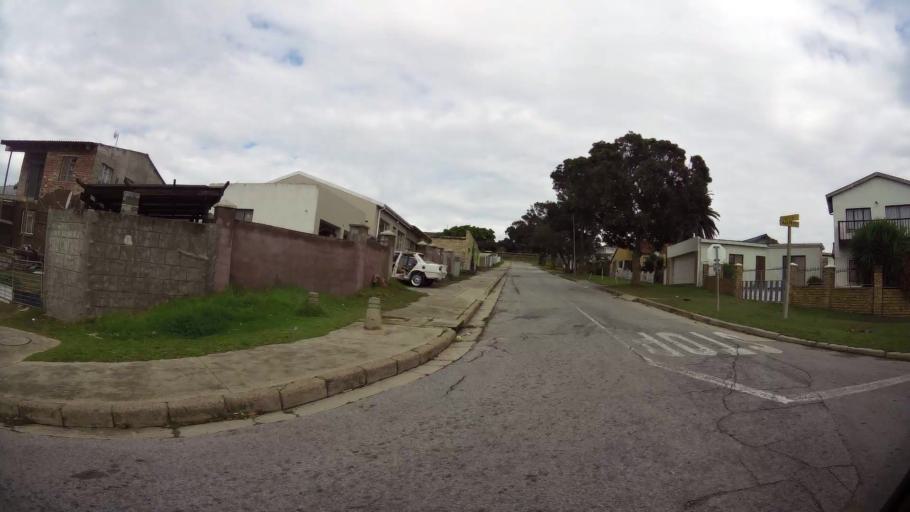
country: ZA
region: Eastern Cape
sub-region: Nelson Mandela Bay Metropolitan Municipality
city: Port Elizabeth
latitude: -33.9405
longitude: 25.5869
